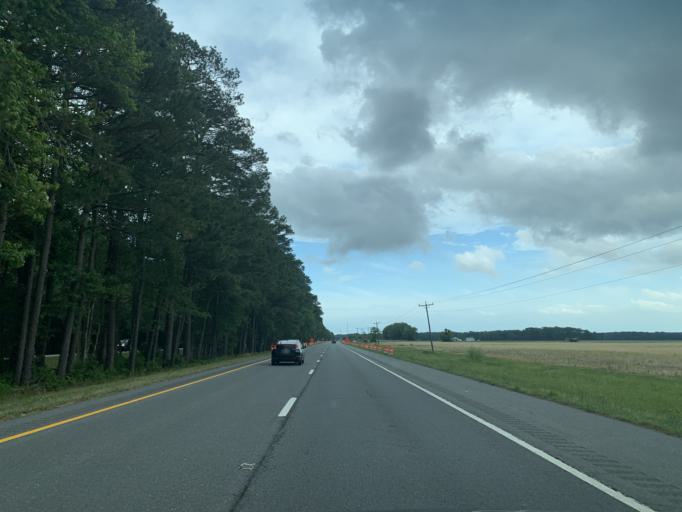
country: US
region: Maryland
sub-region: Worcester County
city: Berlin
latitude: 38.3588
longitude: -75.2520
